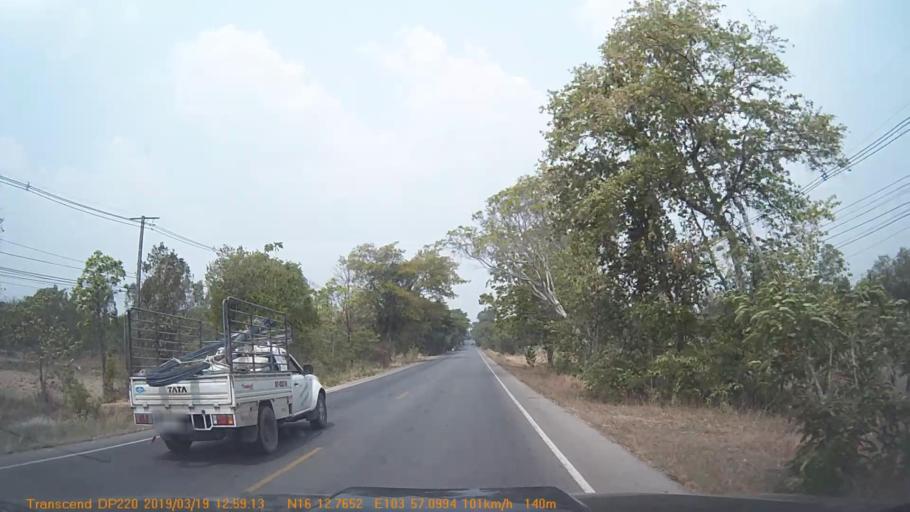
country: TH
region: Roi Et
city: Waeng
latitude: 16.2132
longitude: 103.9517
